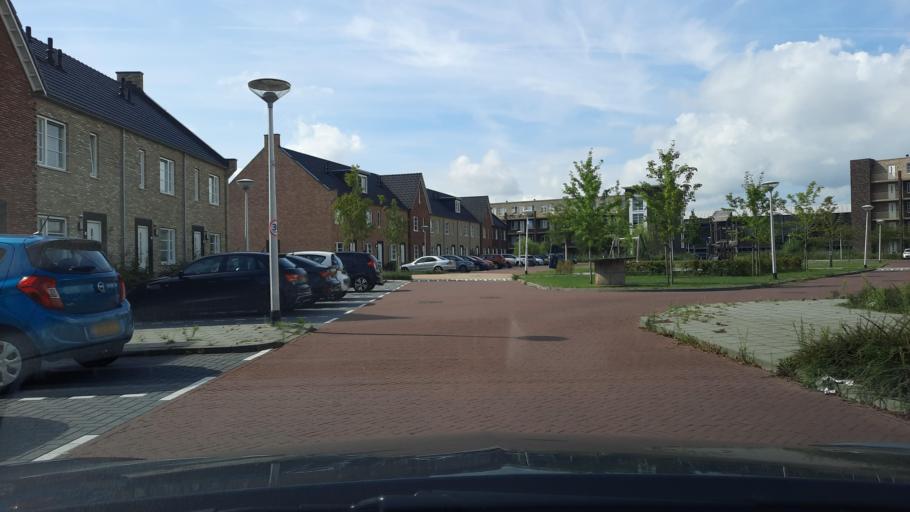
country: NL
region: North Holland
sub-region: Gemeente Aalsmeer
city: Aalsmeer
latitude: 52.2689
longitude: 4.7621
